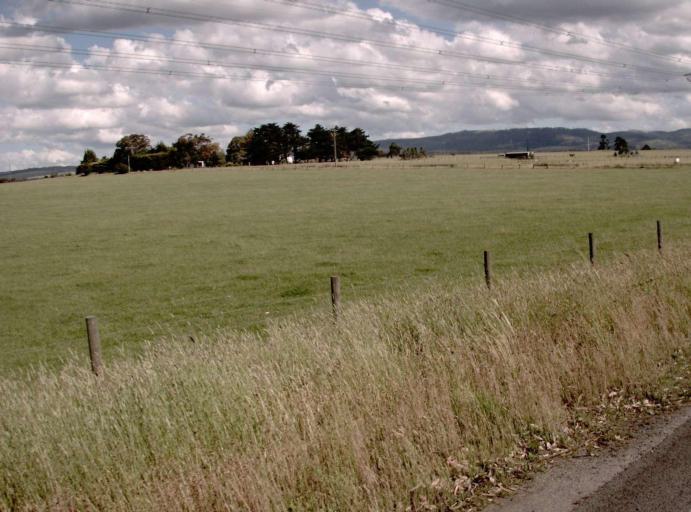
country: AU
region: Victoria
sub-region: Latrobe
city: Morwell
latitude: -38.2653
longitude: 146.4347
